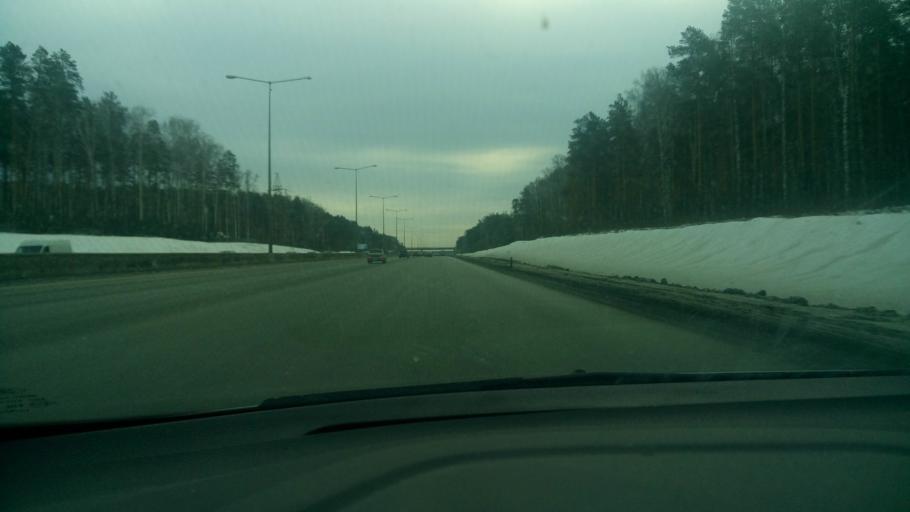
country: RU
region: Sverdlovsk
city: Istok
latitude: 56.7856
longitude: 60.6869
